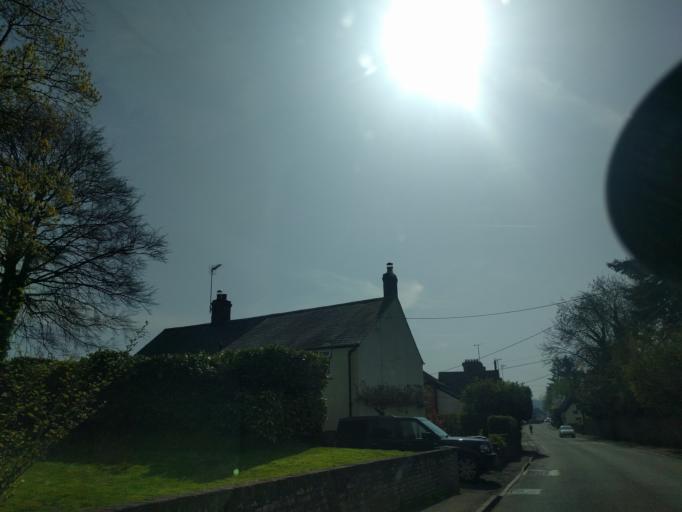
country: GB
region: England
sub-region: Wiltshire
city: Market Lavington
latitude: 51.2857
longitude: -2.0029
